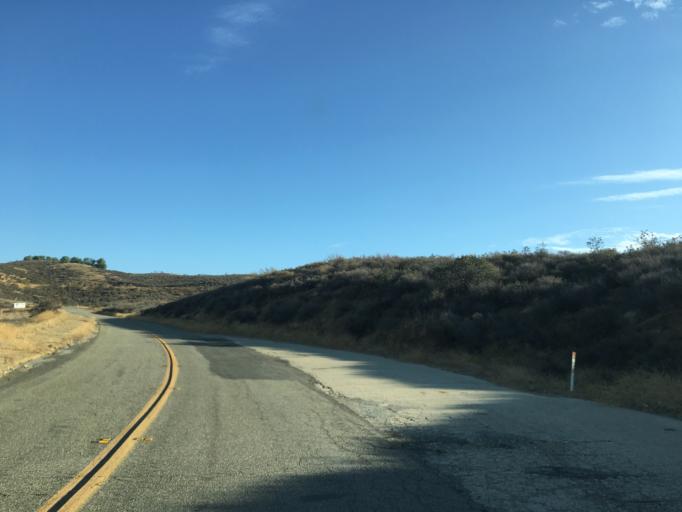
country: US
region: California
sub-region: Los Angeles County
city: Castaic
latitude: 34.5465
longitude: -118.6540
